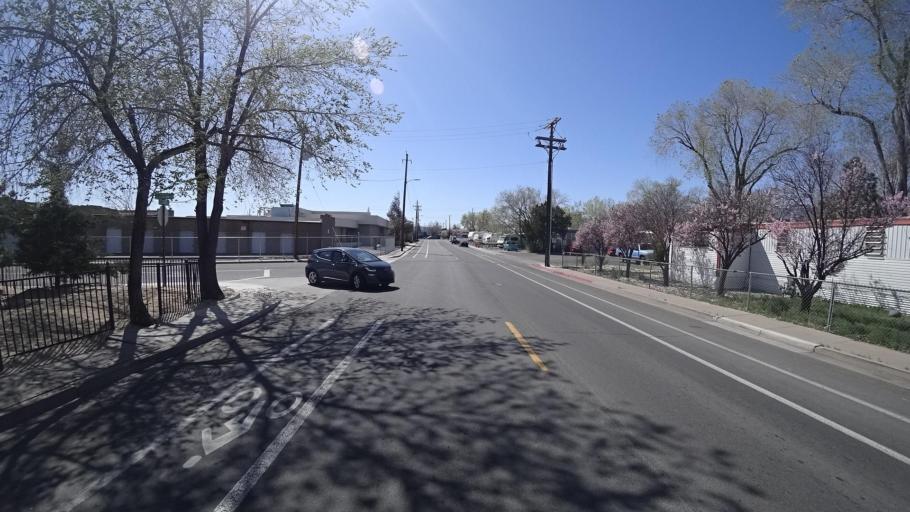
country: US
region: Nevada
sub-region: Washoe County
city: Reno
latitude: 39.4926
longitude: -119.8019
